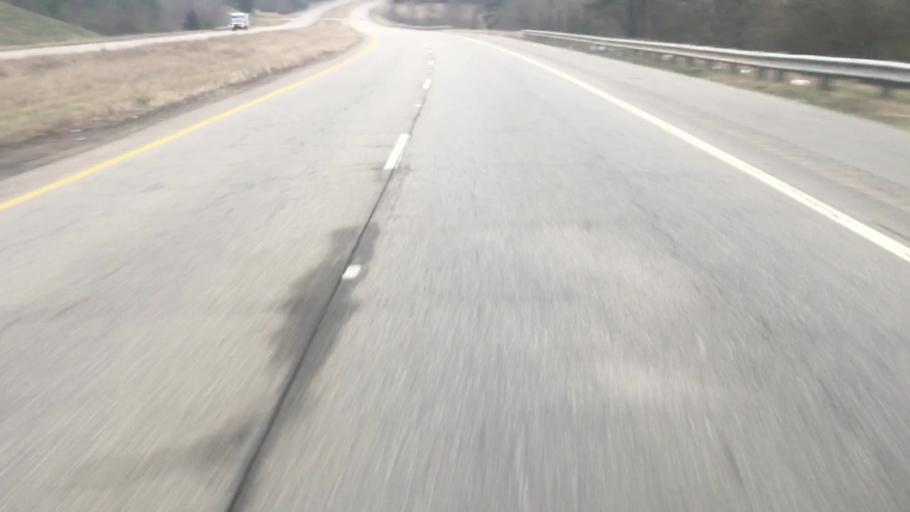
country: US
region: Alabama
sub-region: Walker County
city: Dora
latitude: 33.7945
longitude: -87.1055
